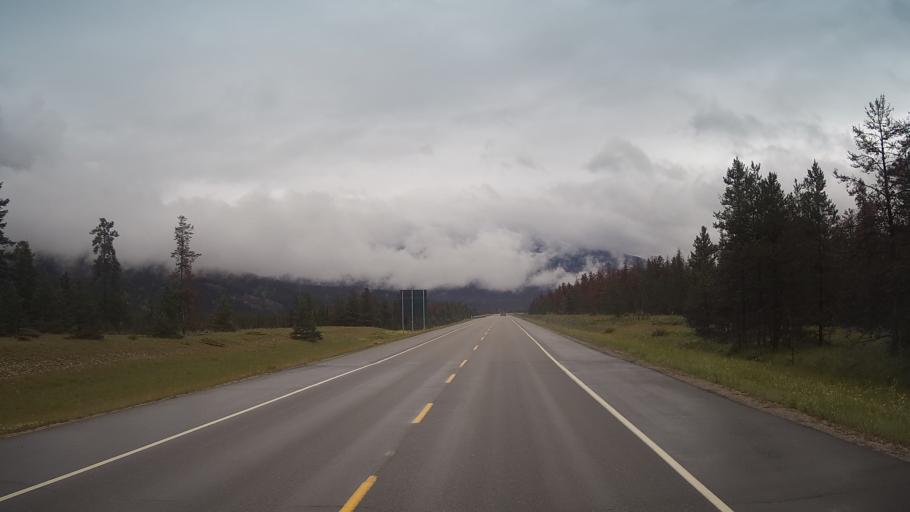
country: CA
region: Alberta
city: Jasper Park Lodge
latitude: 52.9560
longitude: -118.0456
